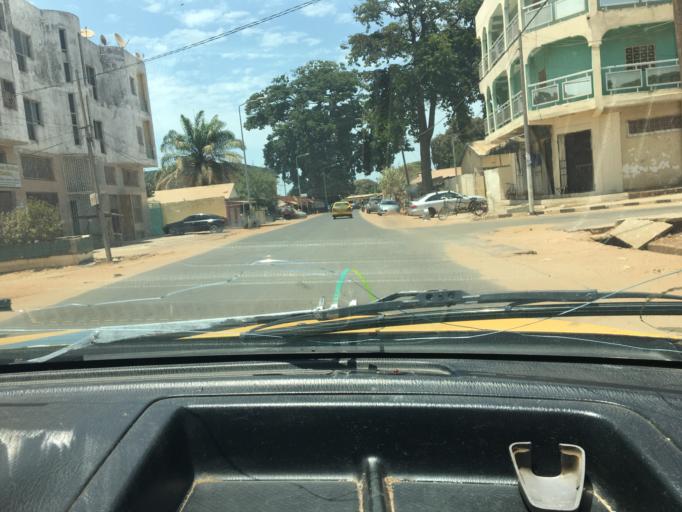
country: GM
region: Banjul
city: Bakau
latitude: 13.4477
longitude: -16.6845
